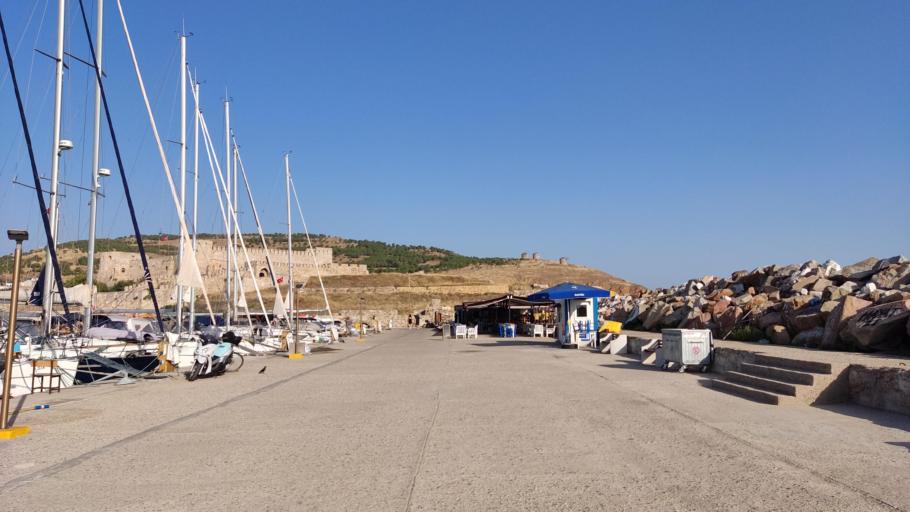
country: TR
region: Canakkale
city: Bozcaada
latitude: 39.8360
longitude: 26.0753
